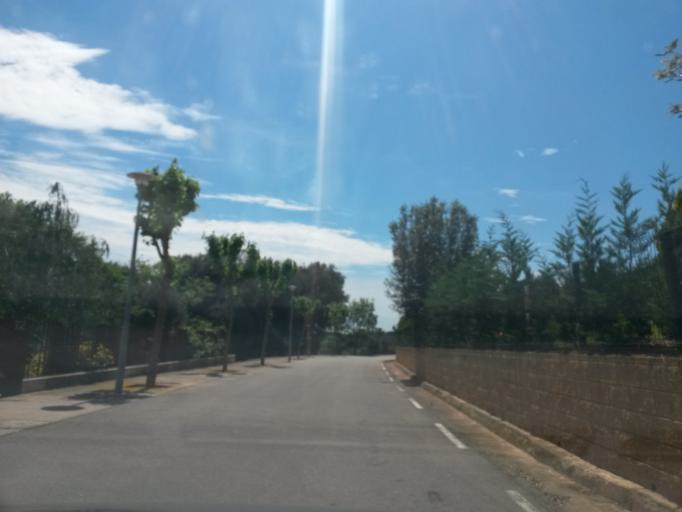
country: ES
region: Catalonia
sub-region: Provincia de Girona
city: Vilablareix
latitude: 41.9601
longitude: 2.7630
